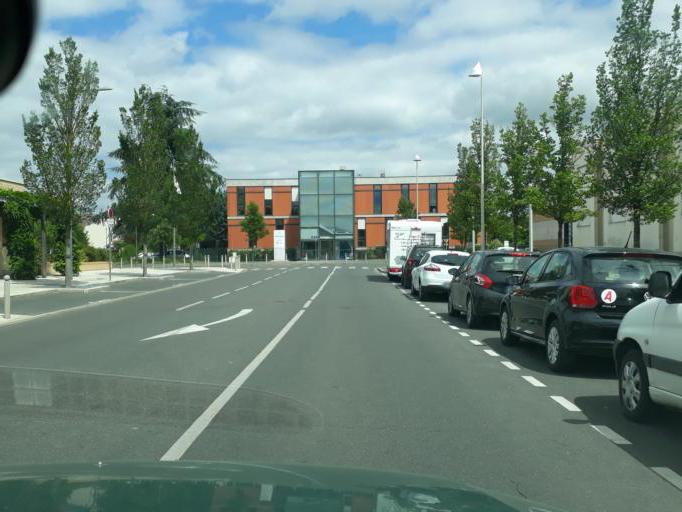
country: FR
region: Centre
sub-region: Departement du Loiret
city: Orleans
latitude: 47.8890
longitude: 1.8980
